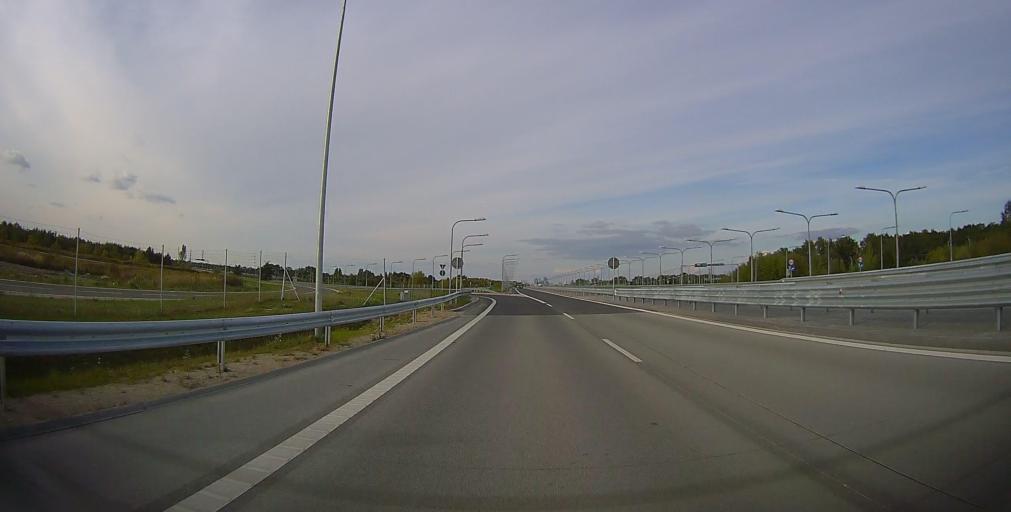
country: PL
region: Masovian Voivodeship
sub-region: Powiat piaseczynski
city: Mysiadlo
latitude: 52.1343
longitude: 20.9889
